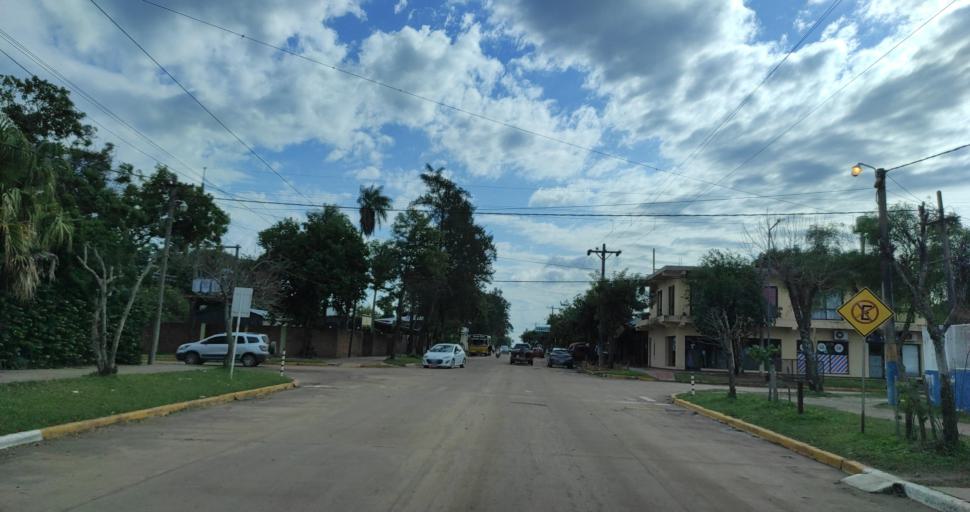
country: AR
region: Corrientes
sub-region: Departamento de Itati
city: Itati
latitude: -27.2714
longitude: -58.2413
